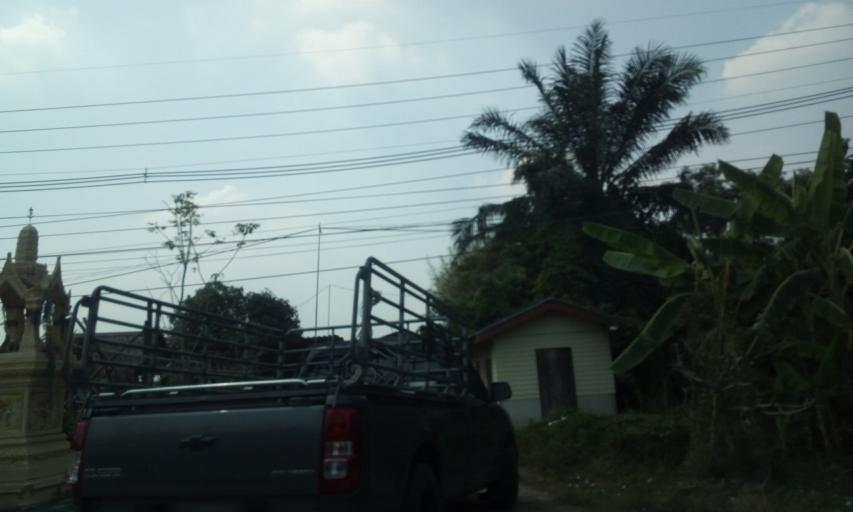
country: TH
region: Nakhon Nayok
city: Ongkharak
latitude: 14.1237
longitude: 100.9429
